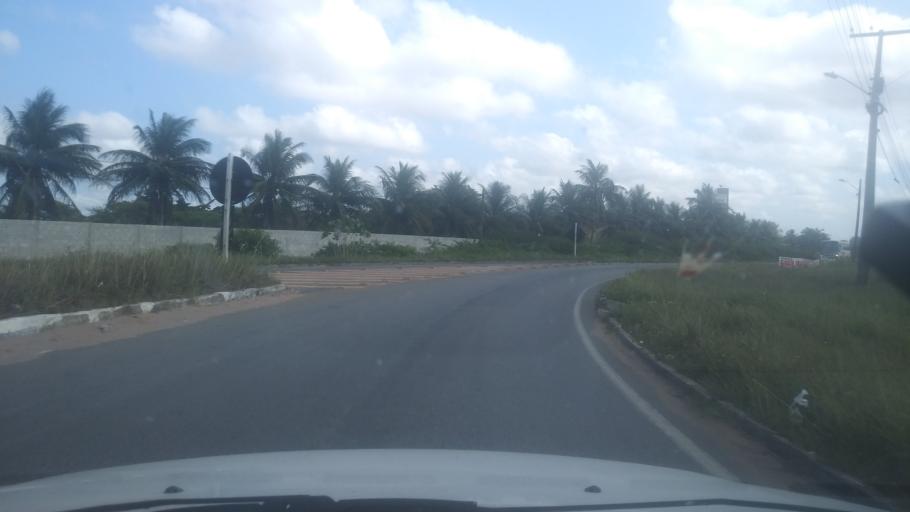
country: BR
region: Rio Grande do Norte
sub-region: Extremoz
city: Extremoz
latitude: -5.7212
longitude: -35.2778
